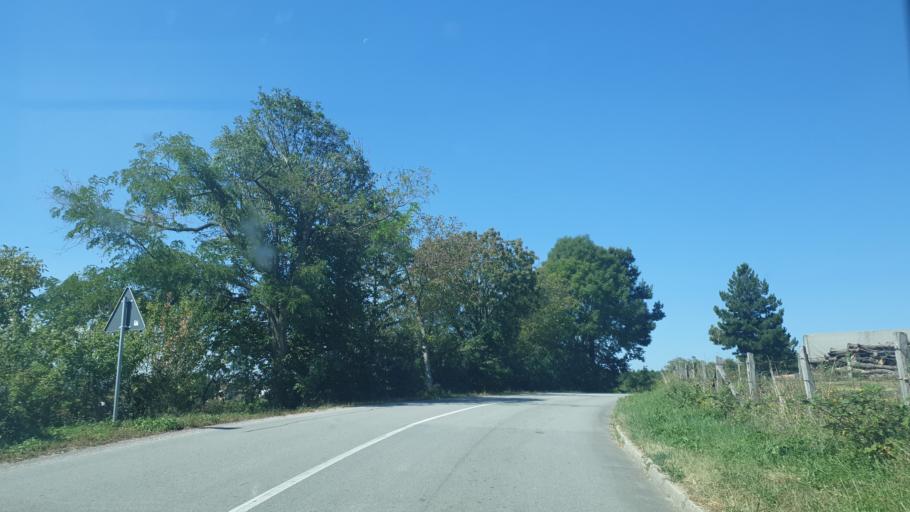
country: RS
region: Central Serbia
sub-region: Kolubarski Okrug
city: Mionica
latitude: 44.1885
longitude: 20.0337
